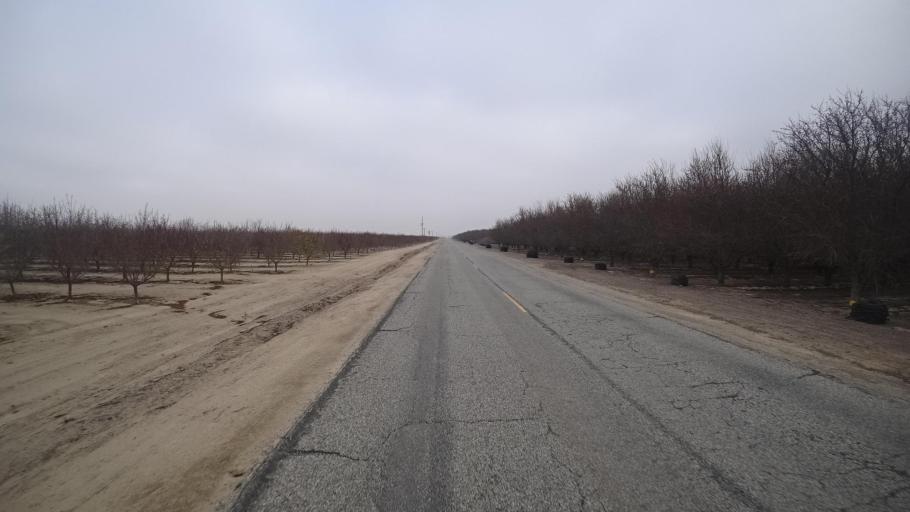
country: US
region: California
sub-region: Kern County
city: Maricopa
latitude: 35.1231
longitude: -119.3523
